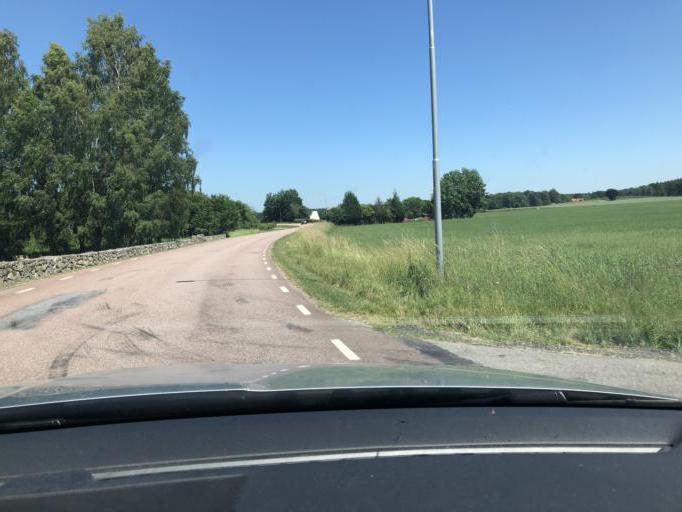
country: SE
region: Blekinge
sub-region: Olofstroms Kommun
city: Jamshog
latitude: 56.1731
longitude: 14.6072
